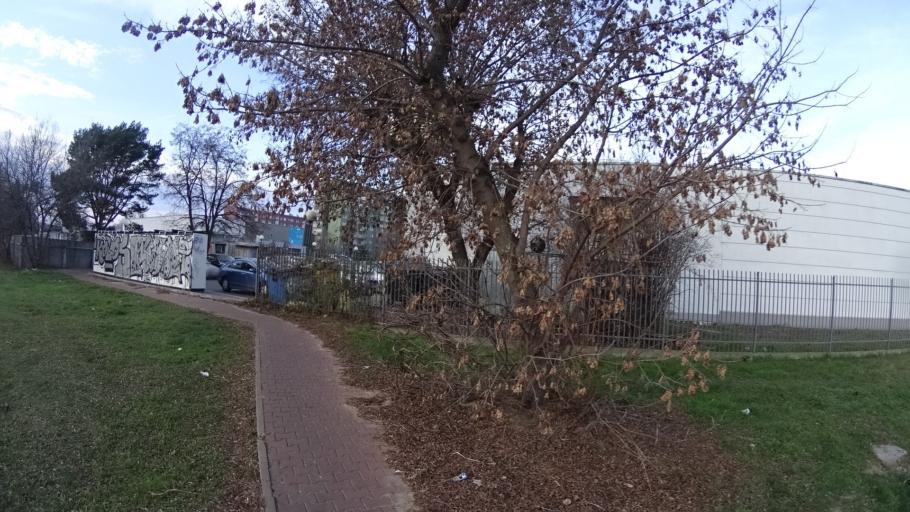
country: PL
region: Masovian Voivodeship
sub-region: Warszawa
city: Bemowo
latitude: 52.2474
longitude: 20.9165
